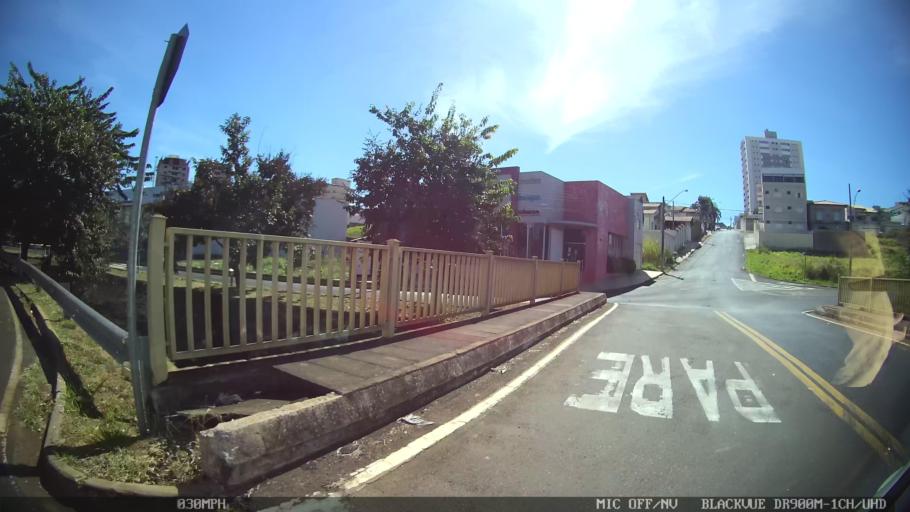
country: BR
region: Sao Paulo
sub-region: Franca
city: Franca
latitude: -20.5516
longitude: -47.4012
